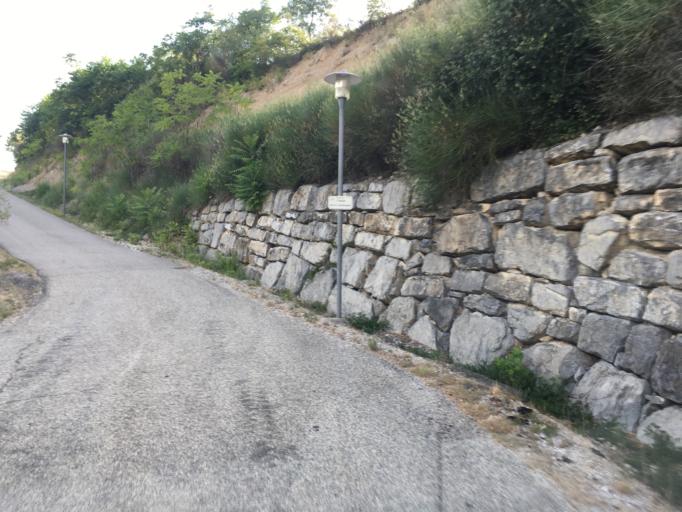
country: FR
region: Rhone-Alpes
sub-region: Departement de la Drome
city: Nyons
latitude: 44.4137
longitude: 5.2627
